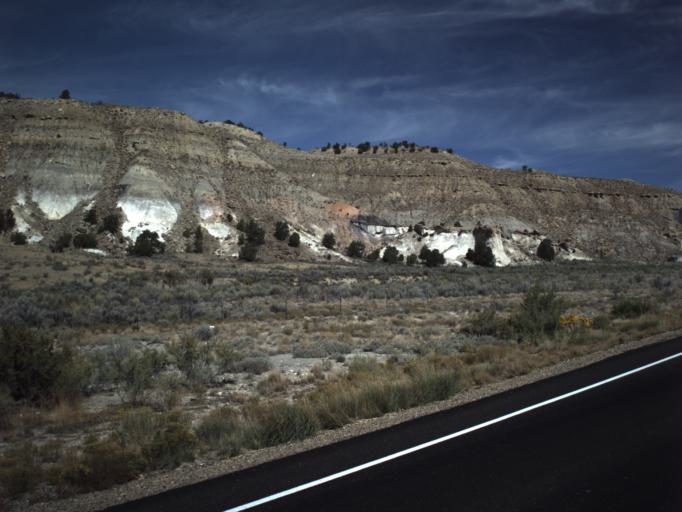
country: US
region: Utah
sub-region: Garfield County
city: Panguitch
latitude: 37.5923
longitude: -111.9811
